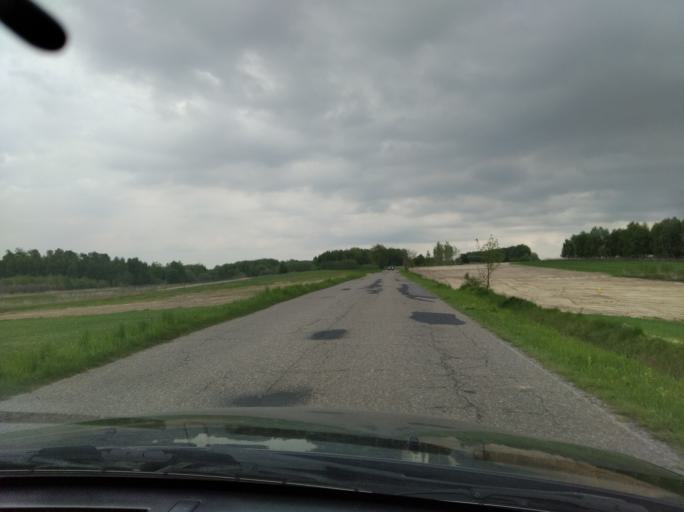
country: PL
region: Lesser Poland Voivodeship
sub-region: Powiat tarnowski
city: Szynwald
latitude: 49.9861
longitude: 21.1263
